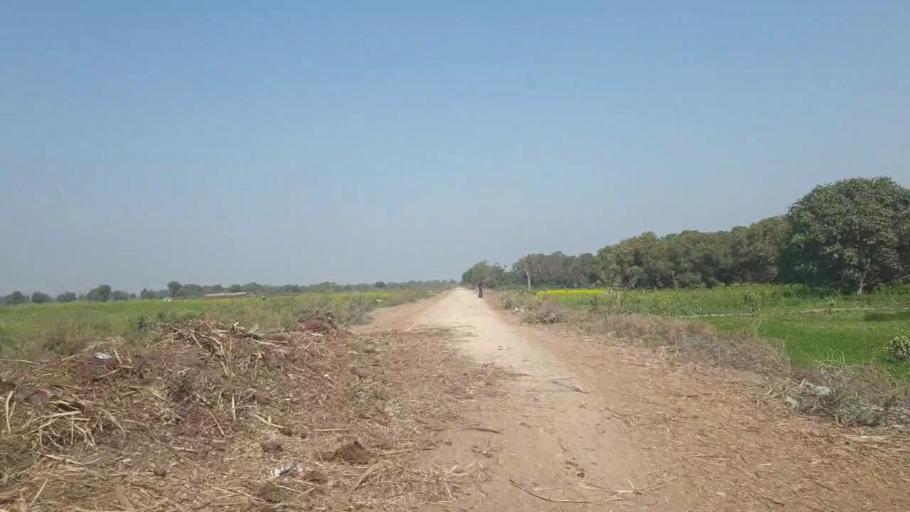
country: PK
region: Sindh
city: Tando Allahyar
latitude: 25.4379
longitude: 68.8499
